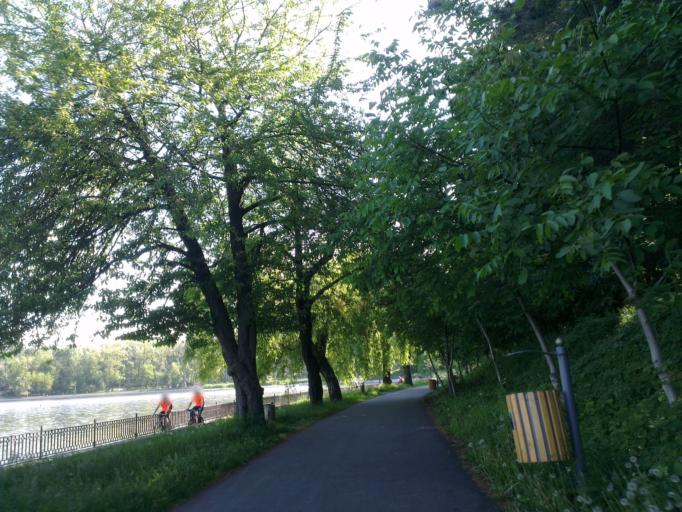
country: MD
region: Chisinau
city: Chisinau
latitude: 47.0167
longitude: 28.8139
